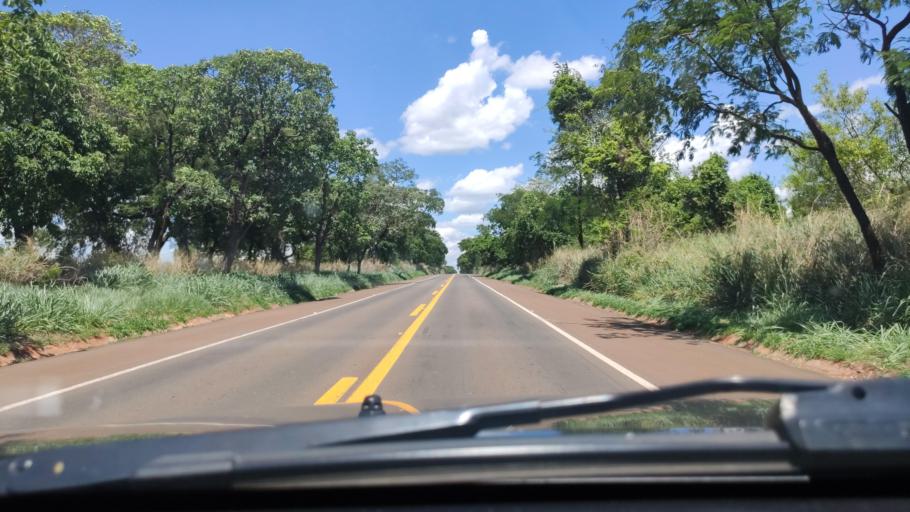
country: BR
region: Sao Paulo
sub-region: Boa Esperanca Do Sul
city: Boa Esperanca do Sul
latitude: -22.0694
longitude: -48.3939
